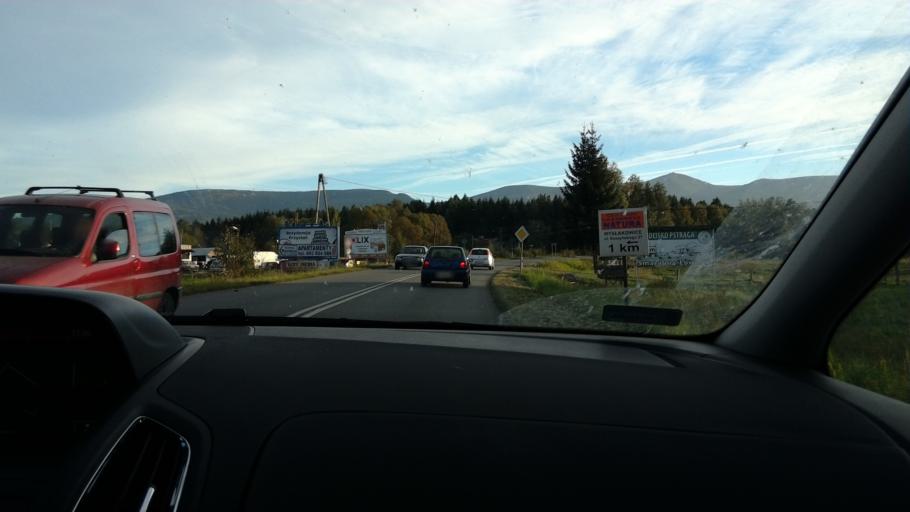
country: PL
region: Lower Silesian Voivodeship
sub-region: Powiat jeleniogorski
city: Myslakowice
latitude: 50.8247
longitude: 15.7785
